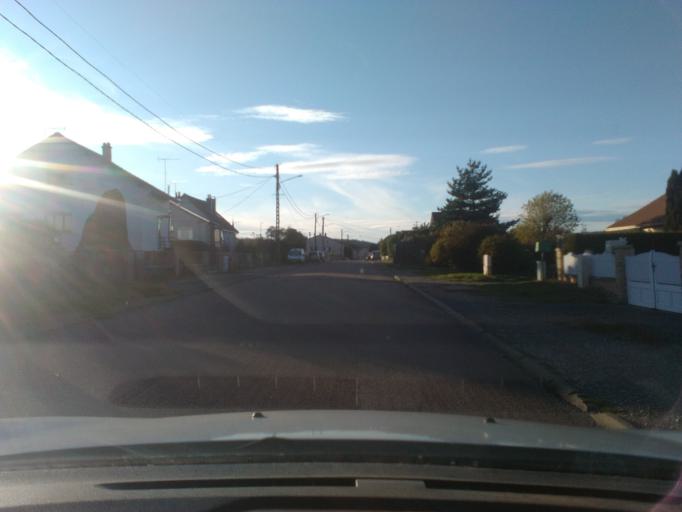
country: FR
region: Lorraine
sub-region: Departement des Vosges
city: Vincey
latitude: 48.3368
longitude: 6.3367
